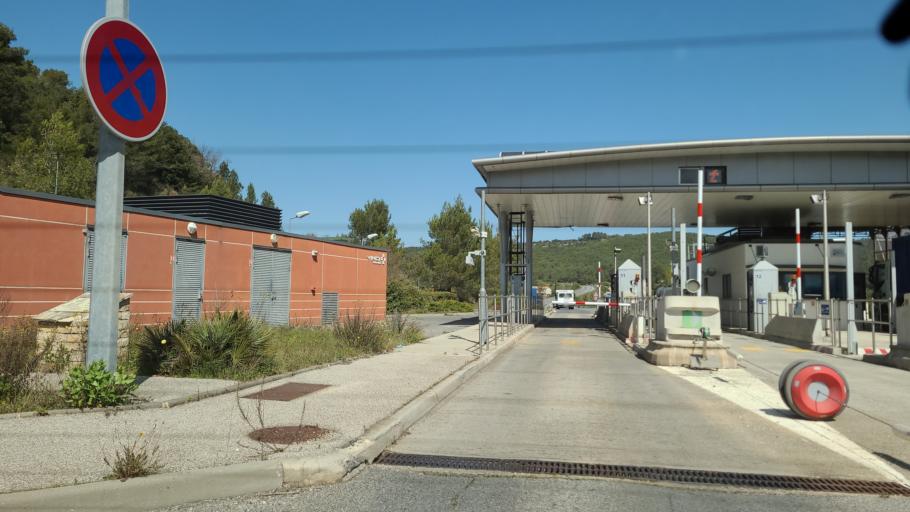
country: FR
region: Provence-Alpes-Cote d'Azur
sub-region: Departement du Var
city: Carnoules
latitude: 43.2932
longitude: 6.2004
